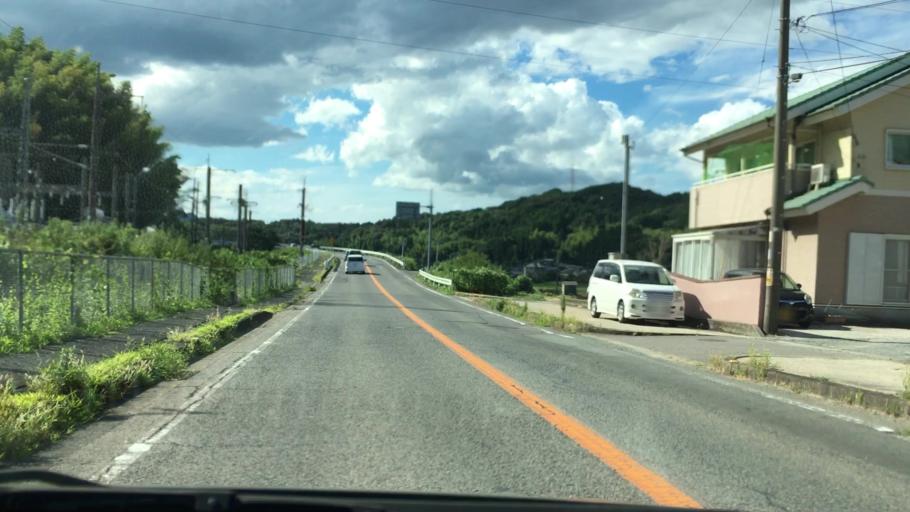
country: JP
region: Saga Prefecture
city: Takeocho-takeo
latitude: 33.1944
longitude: 129.9797
